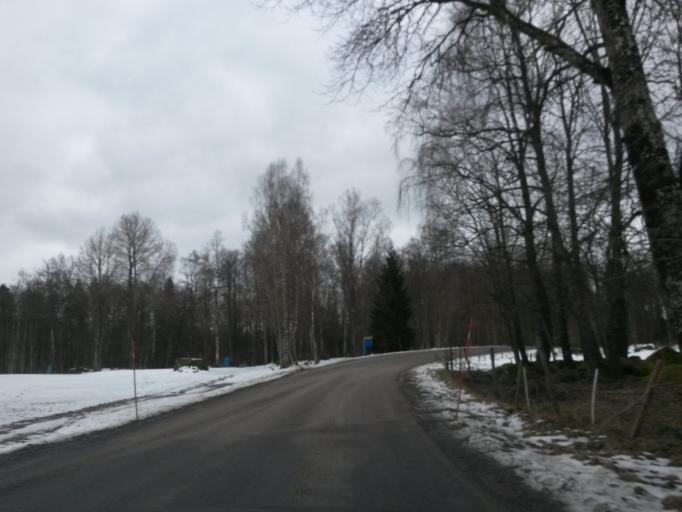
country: SE
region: Vaestra Goetaland
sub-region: Vargarda Kommun
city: Vargarda
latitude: 58.0321
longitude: 12.8653
